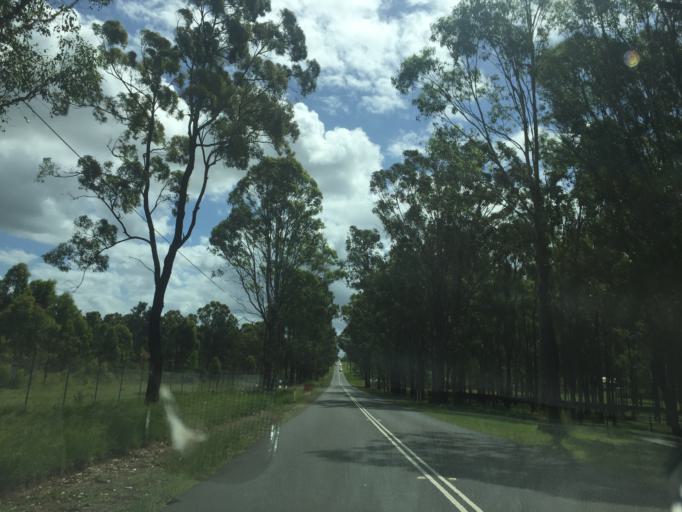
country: AU
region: New South Wales
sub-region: Penrith Municipality
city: Kingswood Park
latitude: -33.7976
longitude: 150.7268
